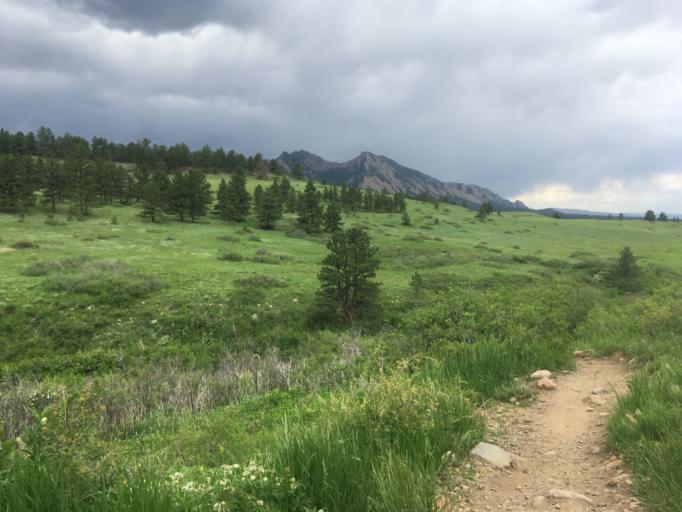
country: US
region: Colorado
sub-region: Boulder County
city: Boulder
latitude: 39.9184
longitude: -105.2597
